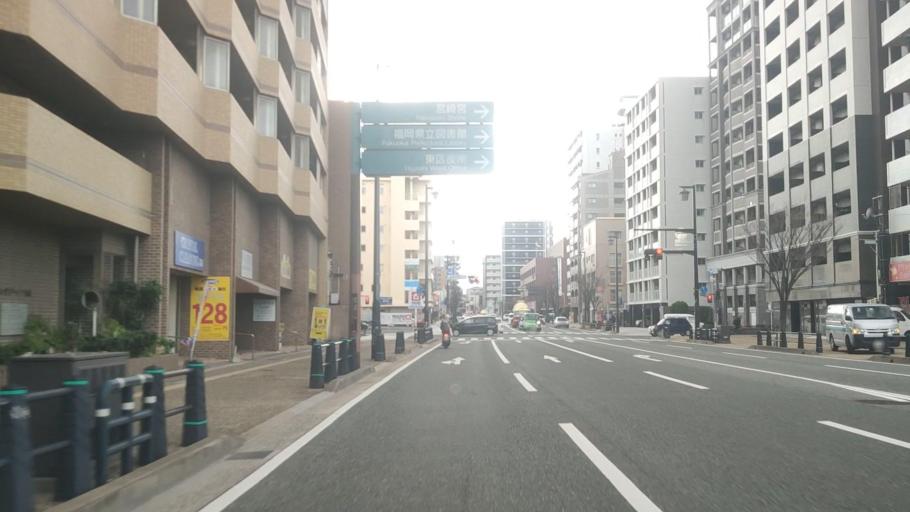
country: JP
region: Fukuoka
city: Fukuoka-shi
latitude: 33.6153
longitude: 130.4255
